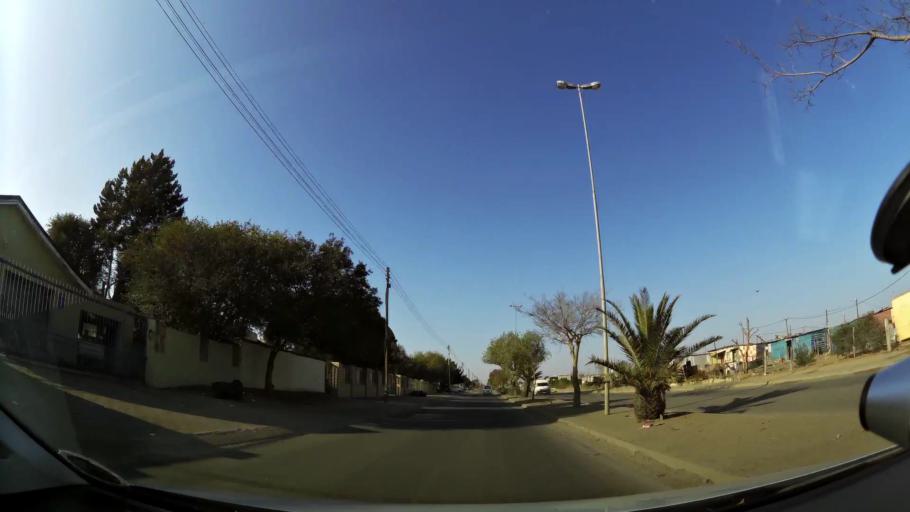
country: ZA
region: Orange Free State
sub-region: Mangaung Metropolitan Municipality
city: Bloemfontein
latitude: -29.1449
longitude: 26.2490
